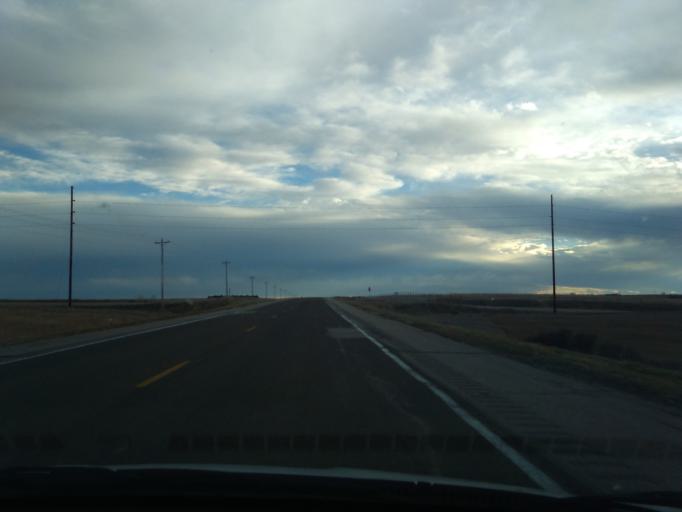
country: US
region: Nebraska
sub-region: Phelps County
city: Holdrege
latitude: 40.3374
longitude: -99.3686
